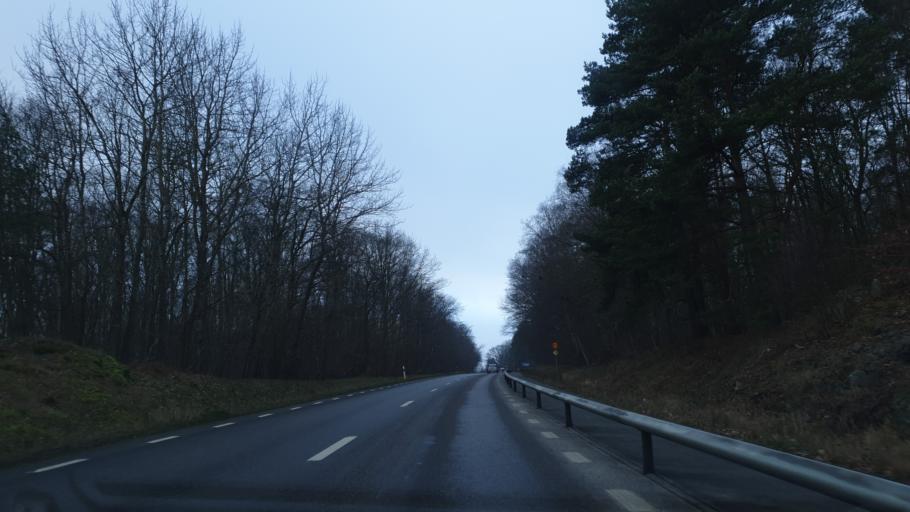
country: SE
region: Blekinge
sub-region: Solvesborgs Kommun
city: Soelvesborg
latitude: 56.0942
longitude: 14.6571
